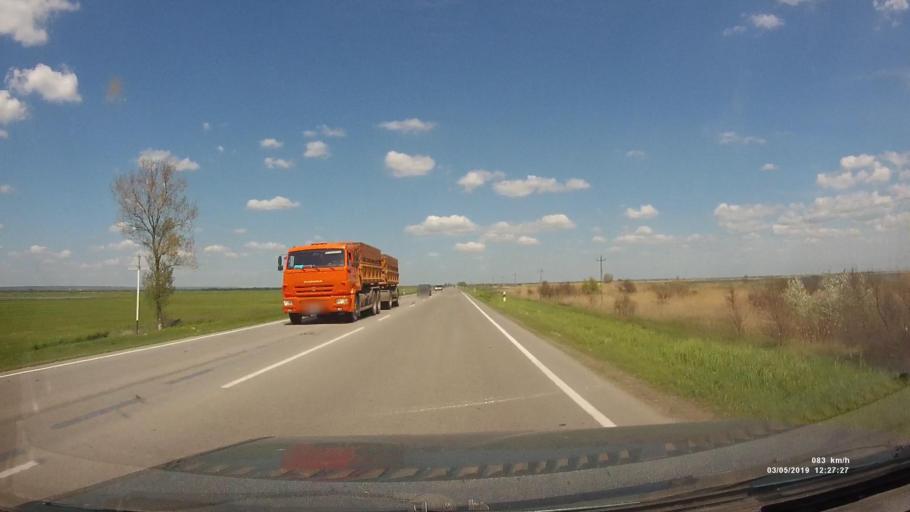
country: RU
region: Rostov
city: Semikarakorsk
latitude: 47.4596
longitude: 40.7211
